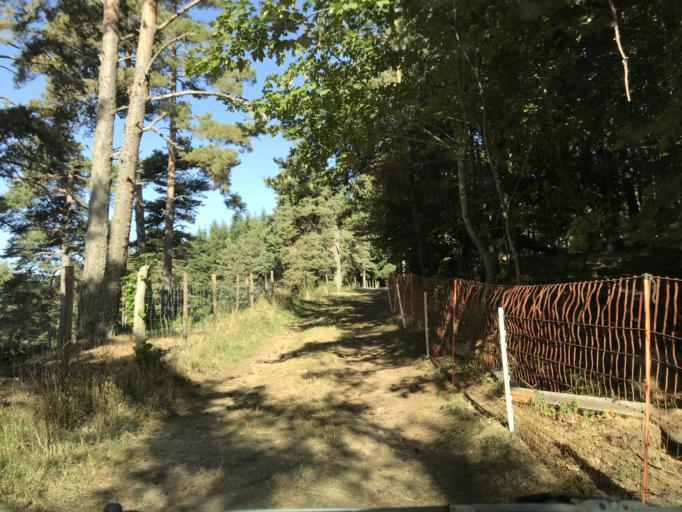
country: FR
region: Rhone-Alpes
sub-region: Departement de l'Ardeche
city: Saint-Agreve
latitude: 45.0280
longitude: 4.4400
